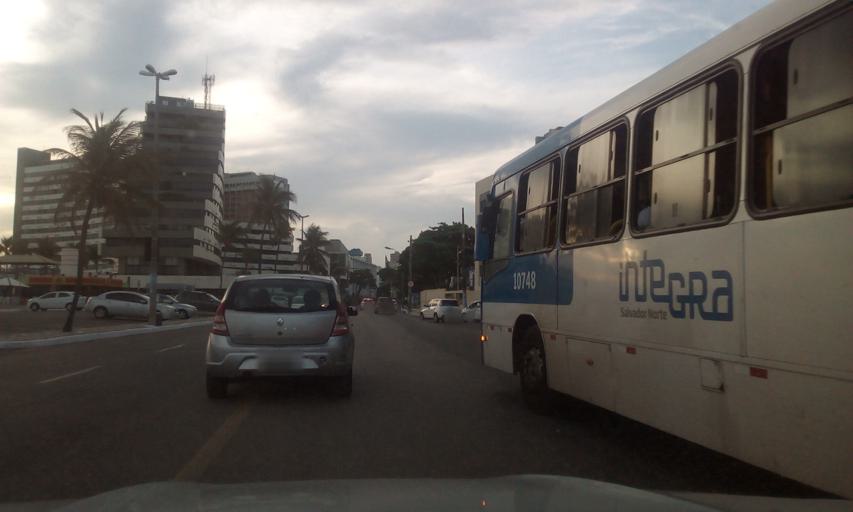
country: BR
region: Bahia
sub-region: Salvador
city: Salvador
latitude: -13.0104
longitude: -38.5102
